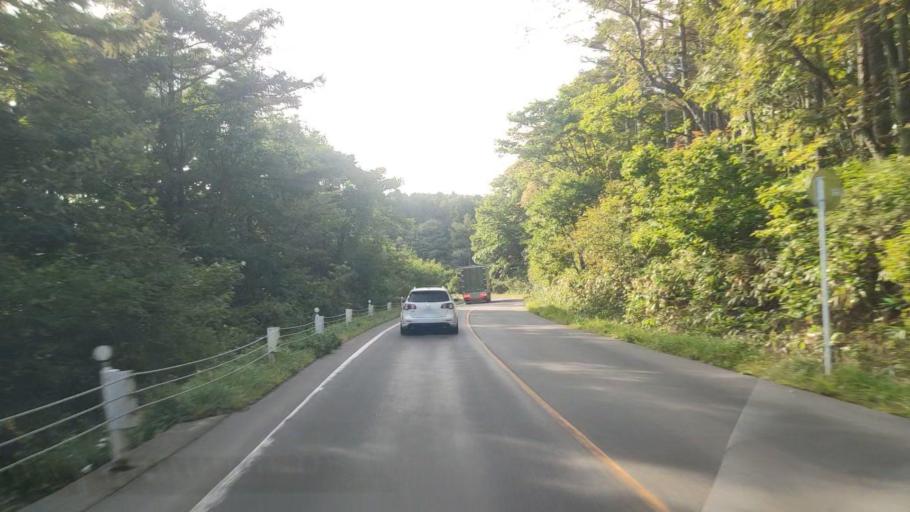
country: JP
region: Nagano
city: Ueda
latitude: 36.4900
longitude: 138.4023
